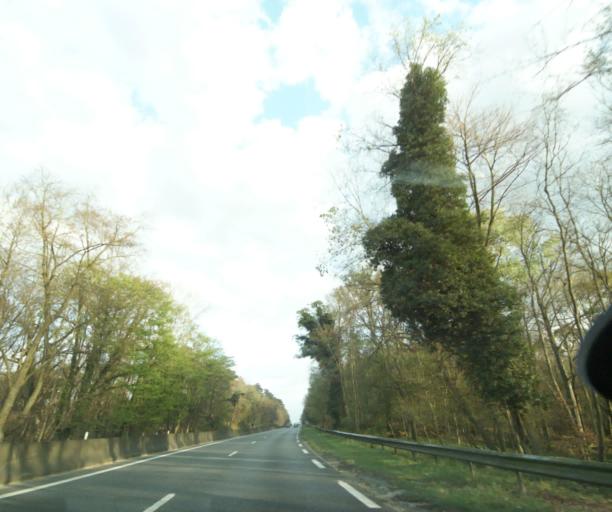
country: FR
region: Ile-de-France
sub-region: Departement de Seine-et-Marne
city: Barbizon
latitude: 48.4405
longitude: 2.6512
